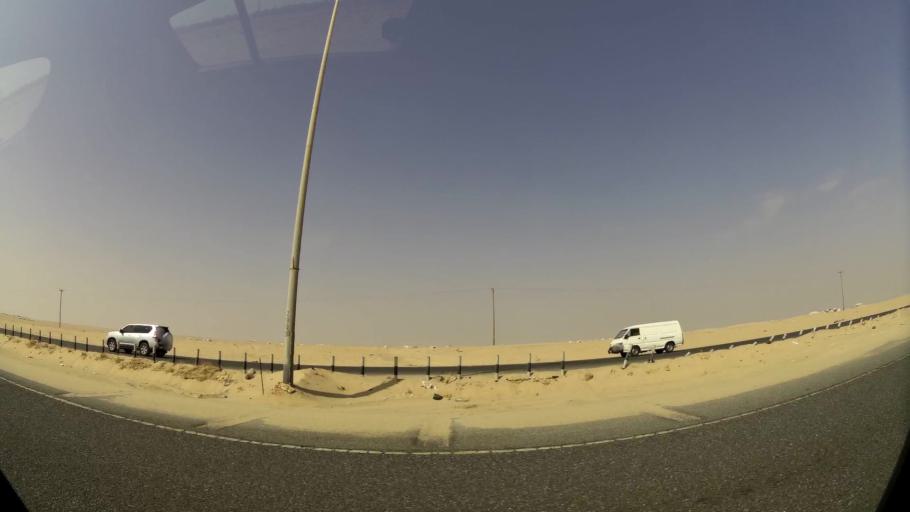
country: KW
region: Al Ahmadi
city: Al Wafrah
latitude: 28.8150
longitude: 48.0453
